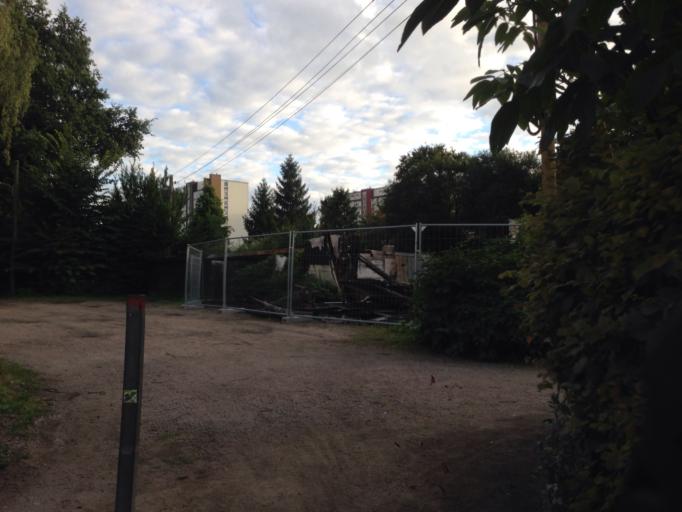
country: DE
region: Hamburg
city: Marienthal
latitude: 53.5892
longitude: 10.0883
